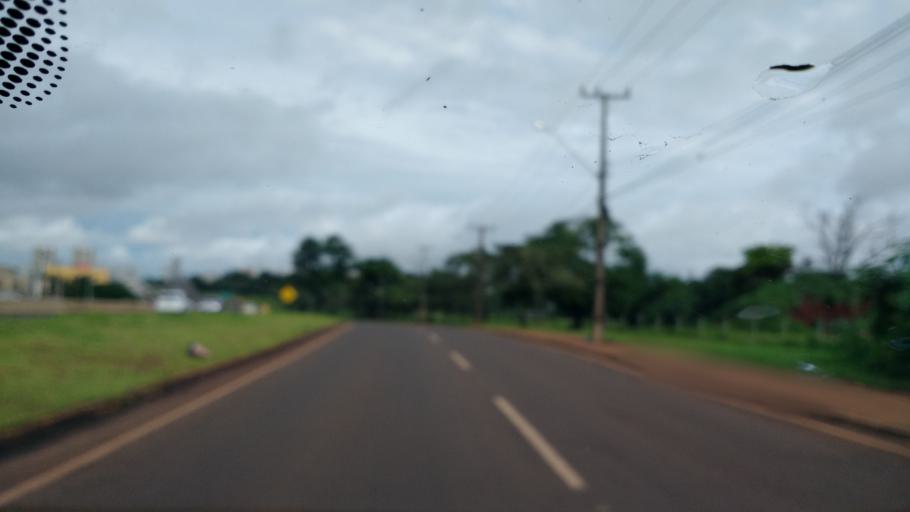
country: BR
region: Parana
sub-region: Londrina
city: Londrina
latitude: -23.3203
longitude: -51.2078
